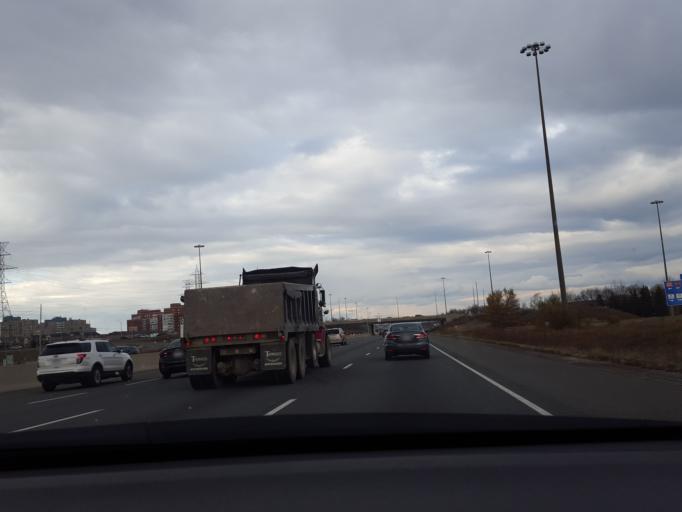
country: CA
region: Ontario
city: Mississauga
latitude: 43.5983
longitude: -79.6469
